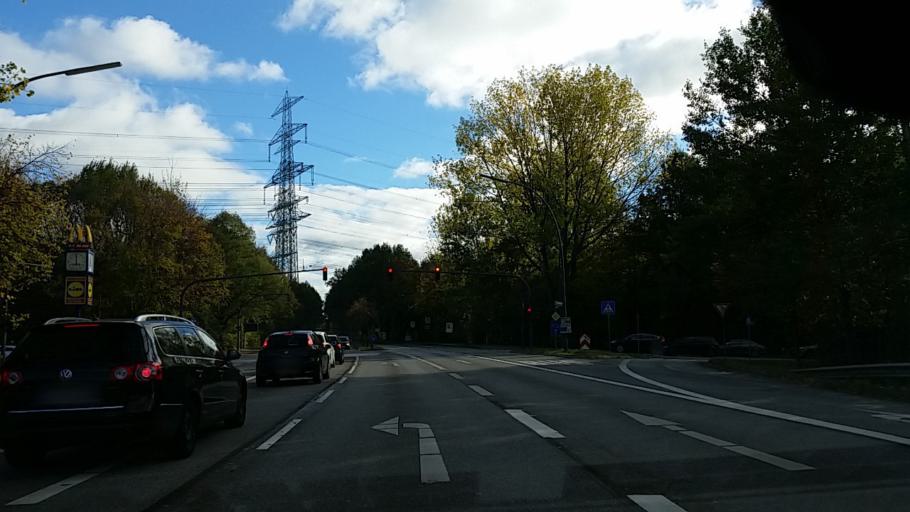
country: DE
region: Schleswig-Holstein
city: Oststeinbek
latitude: 53.5430
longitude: 10.1516
